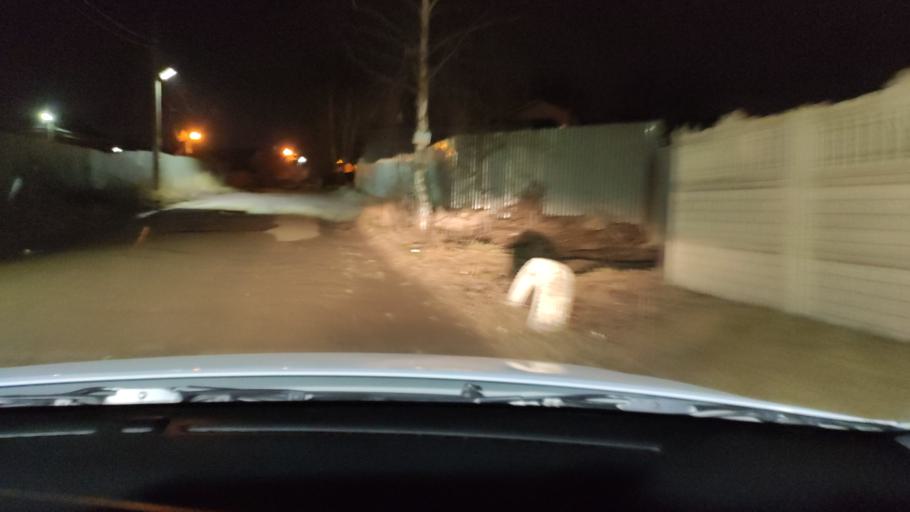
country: RU
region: Tatarstan
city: Vysokaya Gora
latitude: 55.8526
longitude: 49.2376
